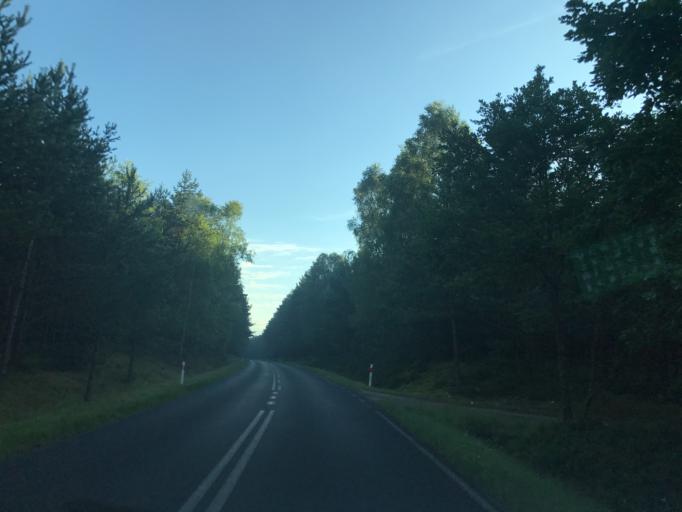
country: PL
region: West Pomeranian Voivodeship
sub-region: Powiat koszalinski
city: Sianow
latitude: 54.0883
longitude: 16.3448
